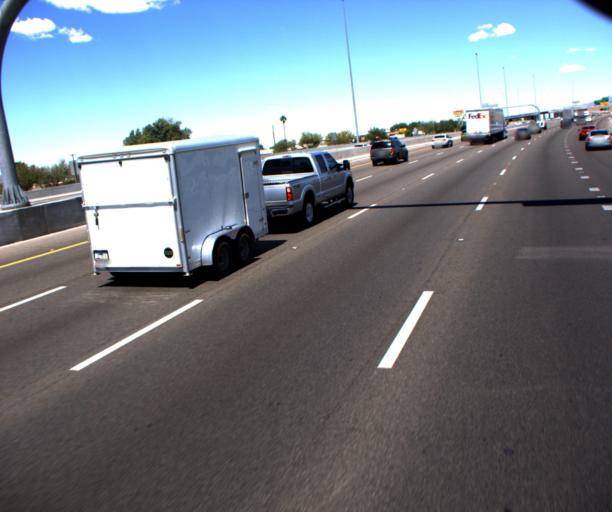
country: US
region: Arizona
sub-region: Pima County
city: Flowing Wells
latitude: 32.2642
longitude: -111.0063
